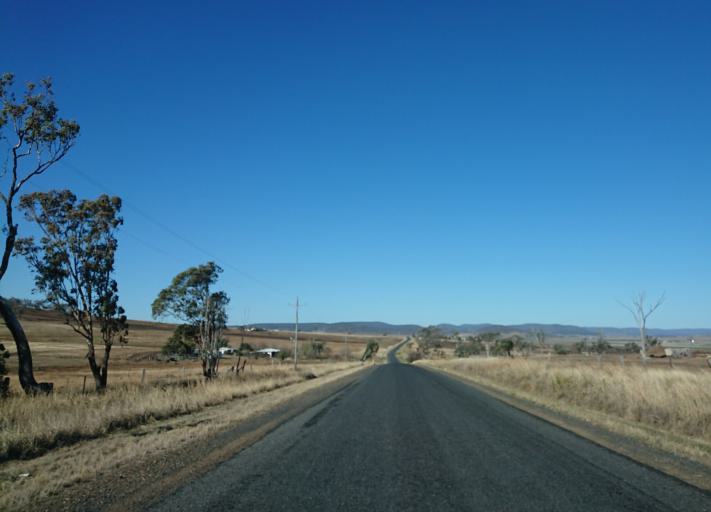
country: AU
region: Queensland
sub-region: Toowoomba
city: Top Camp
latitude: -27.8091
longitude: 151.9536
